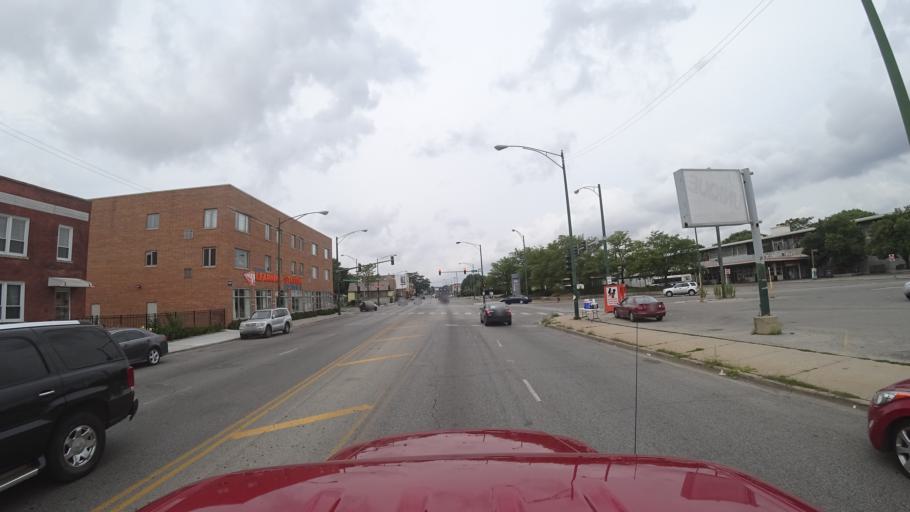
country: US
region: Illinois
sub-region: Cook County
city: Chicago
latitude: 41.8293
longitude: -87.6796
